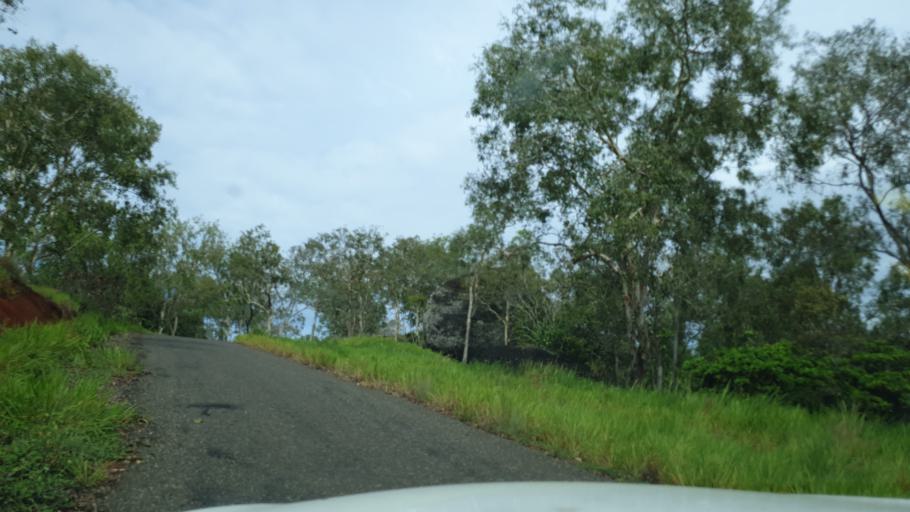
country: PG
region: National Capital
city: Port Moresby
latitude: -9.4342
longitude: 147.3897
